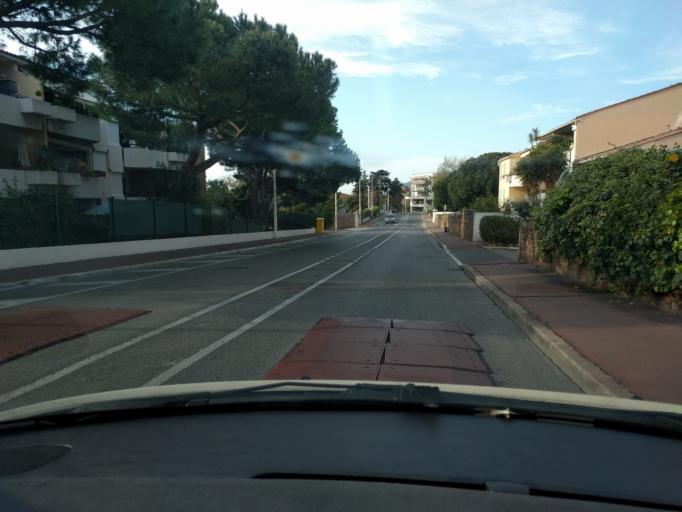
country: FR
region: Provence-Alpes-Cote d'Azur
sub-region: Departement des Alpes-Maritimes
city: Cannes
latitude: 43.5585
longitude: 6.9738
